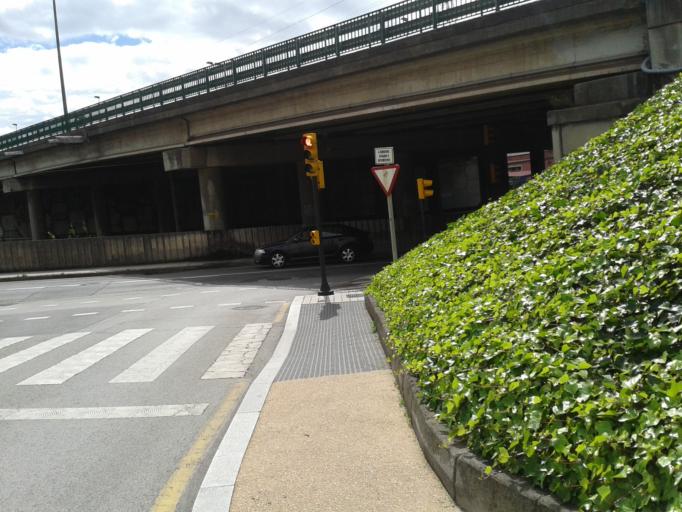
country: ES
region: Asturias
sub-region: Province of Asturias
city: Natahoyo
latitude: 43.5366
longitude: -5.6895
